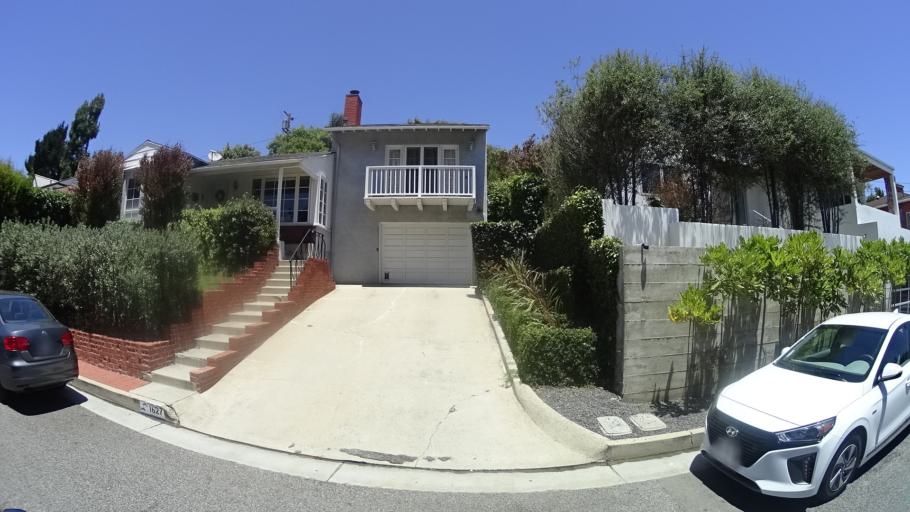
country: US
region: California
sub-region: Los Angeles County
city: Santa Monica
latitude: 34.0080
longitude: -118.4650
